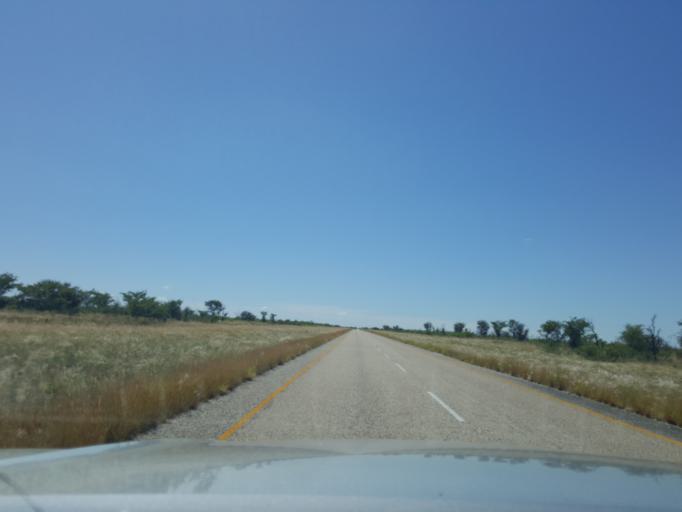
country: BW
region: Central
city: Gweta
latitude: -20.2311
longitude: 24.9557
